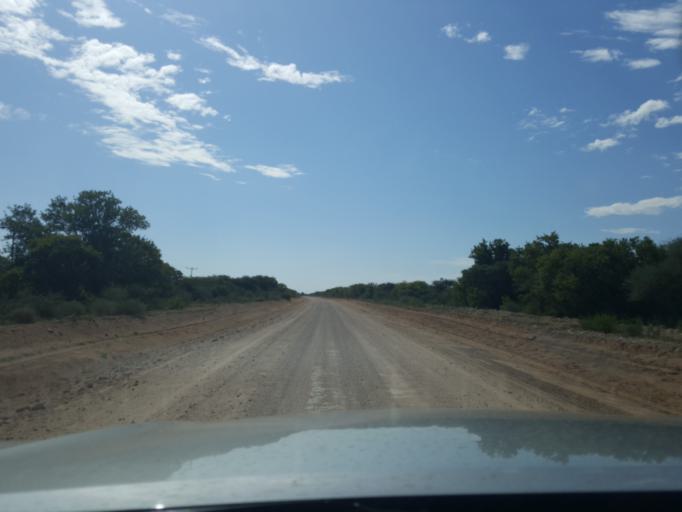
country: BW
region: Kweneng
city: Khudumelapye
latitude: -23.7990
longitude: 24.8010
